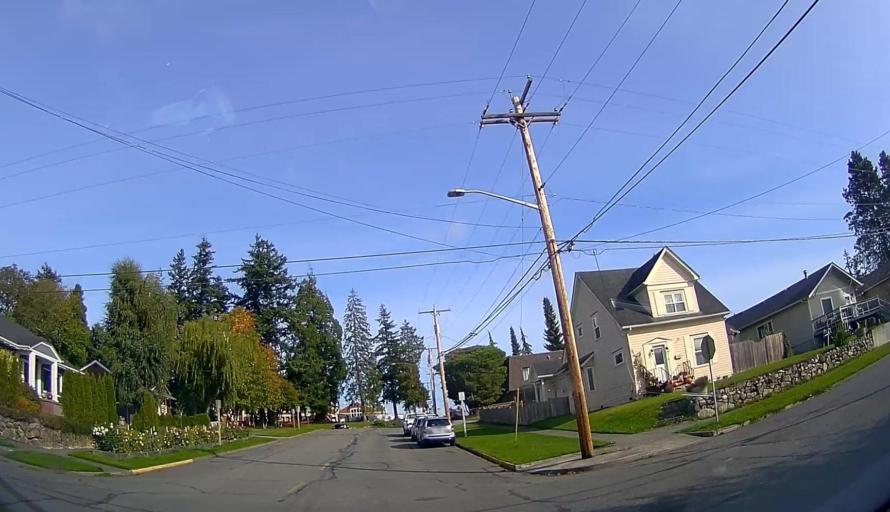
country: US
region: Washington
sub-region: Skagit County
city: Mount Vernon
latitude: 48.4232
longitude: -122.3308
